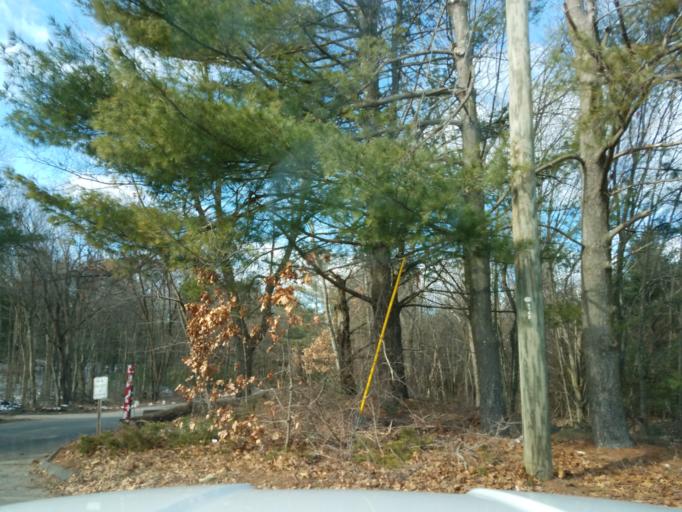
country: US
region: Connecticut
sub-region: Hartford County
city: Bristol
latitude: 41.6379
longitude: -72.9049
